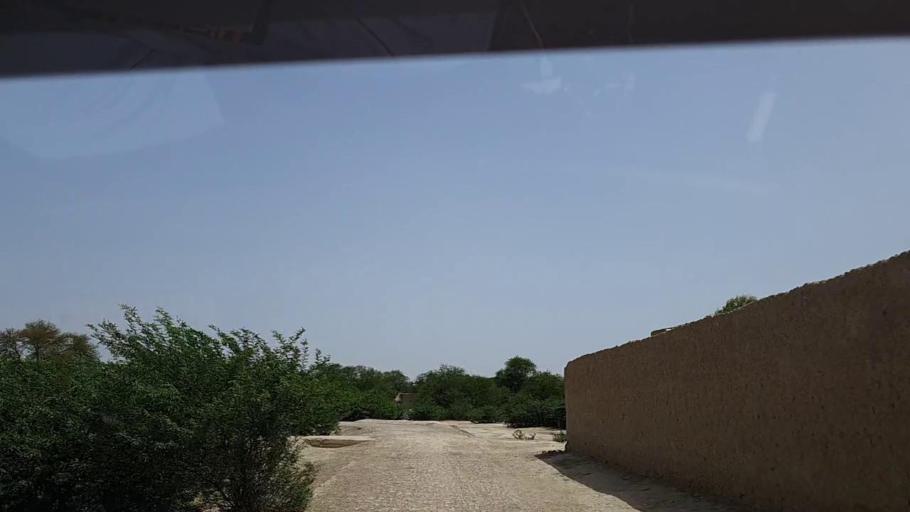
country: PK
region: Sindh
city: Johi
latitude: 26.7144
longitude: 67.6517
